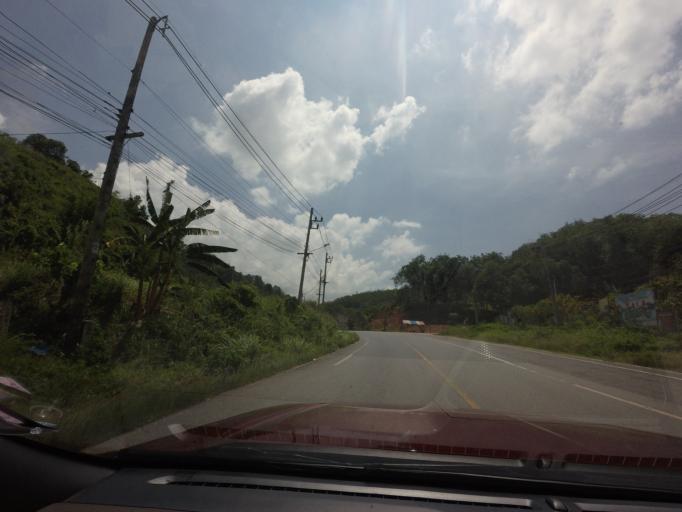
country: TH
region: Yala
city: Betong
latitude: 5.7905
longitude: 101.0724
